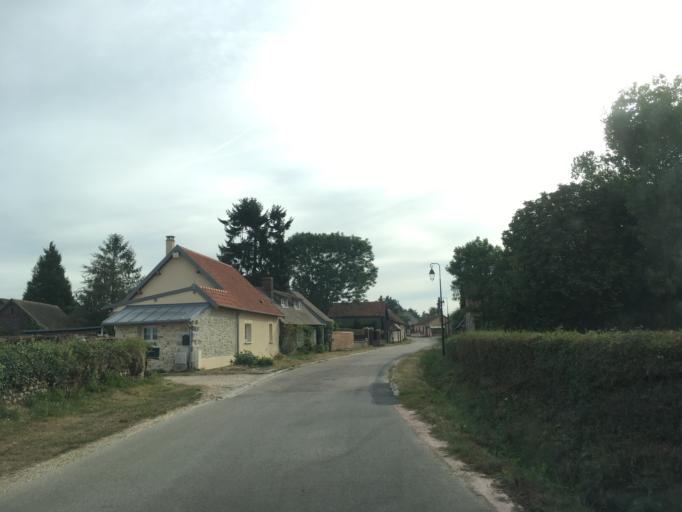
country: FR
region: Ile-de-France
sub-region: Departement des Yvelines
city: Limetz-Villez
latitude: 49.1133
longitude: 1.5577
